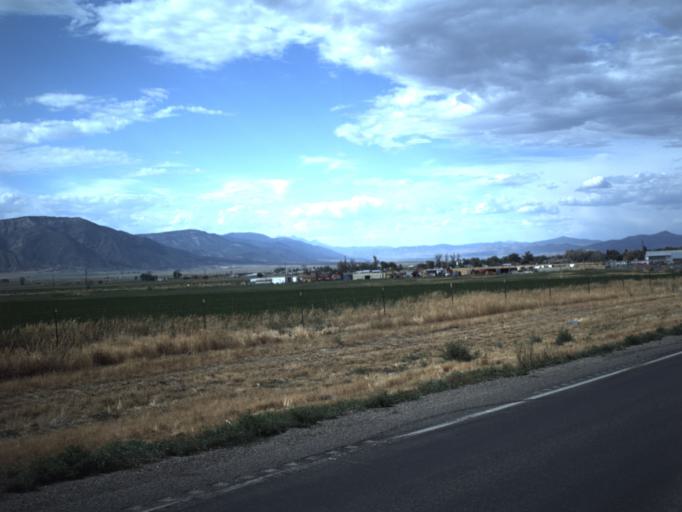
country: US
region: Utah
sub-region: Sanpete County
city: Ephraim
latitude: 39.3418
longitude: -111.5932
